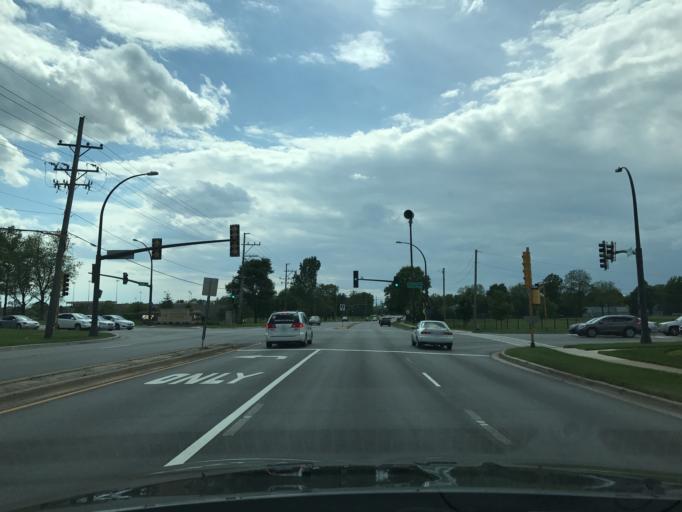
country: US
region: Illinois
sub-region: DuPage County
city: Lisle
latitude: 41.7823
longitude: -88.0919
